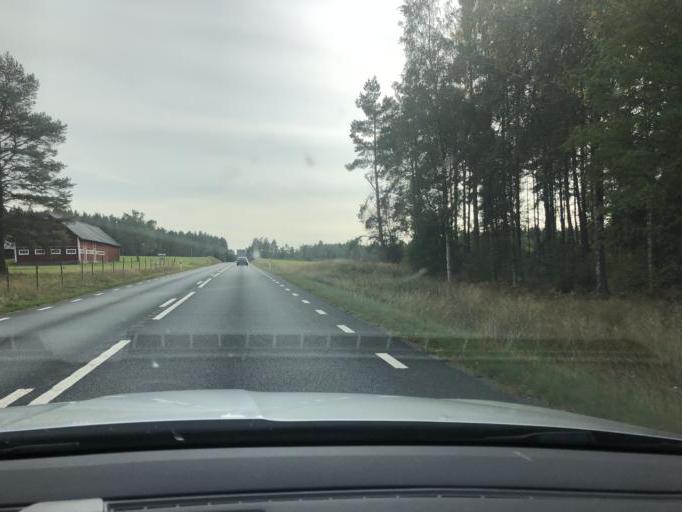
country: SE
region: Joenkoeping
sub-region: Vetlanda Kommun
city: Ekenassjon
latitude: 57.5403
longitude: 14.9927
